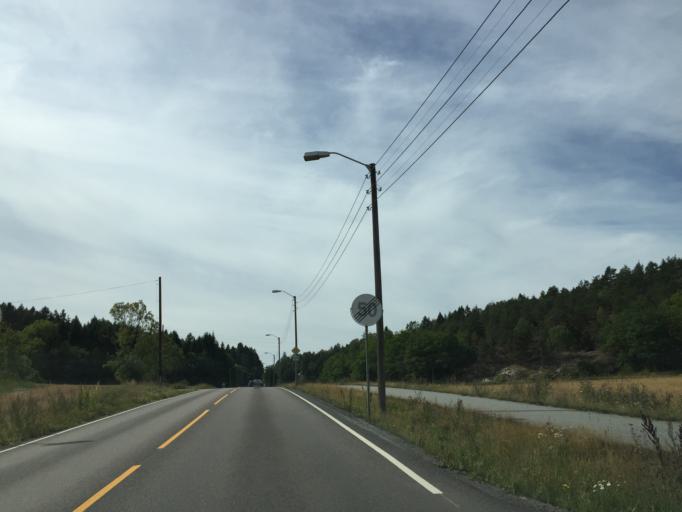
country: NO
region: Ostfold
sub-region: Fredrikstad
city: Fredrikstad
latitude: 59.1917
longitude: 10.9379
